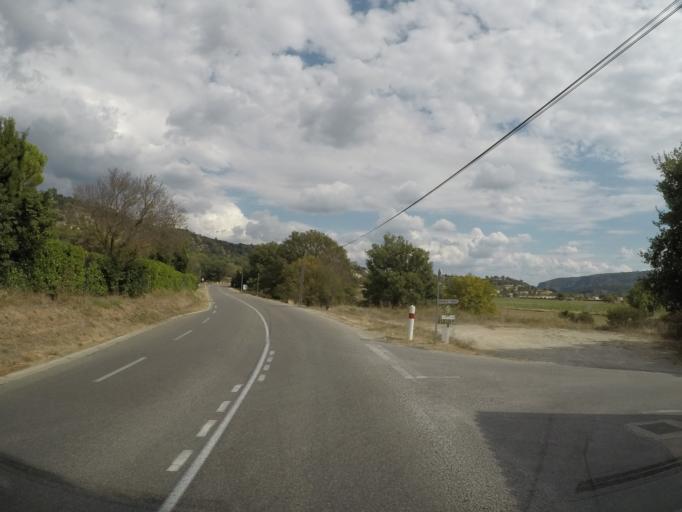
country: FR
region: Provence-Alpes-Cote d'Azur
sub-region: Departement des Alpes-de-Haute-Provence
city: Greoux-les-Bains
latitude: 43.7556
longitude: 5.8677
